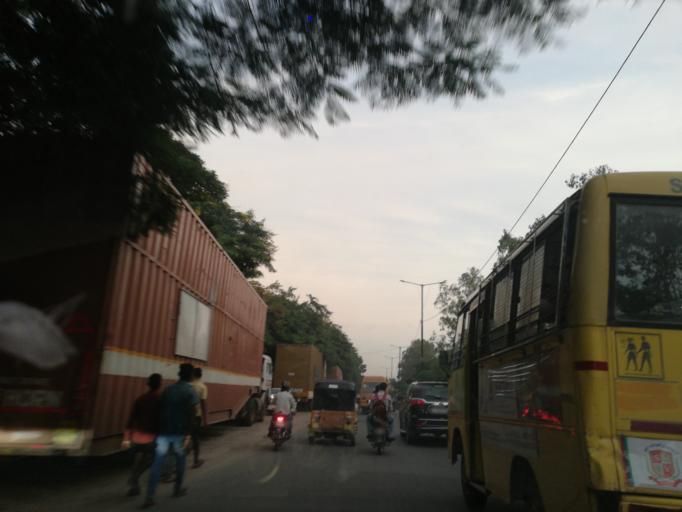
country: IN
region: Telangana
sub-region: Rangareddi
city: Kukatpalli
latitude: 17.5116
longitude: 78.3614
